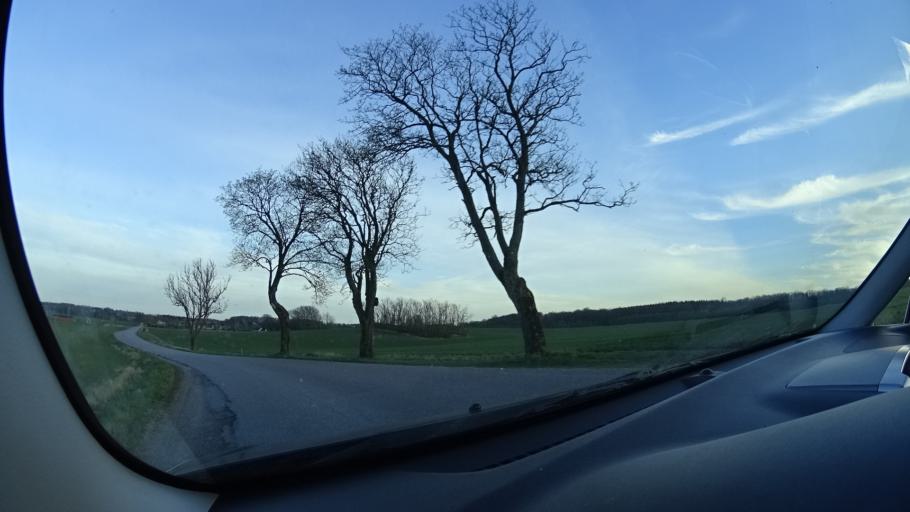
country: SE
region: Skane
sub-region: Eslovs Kommun
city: Stehag
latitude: 55.9111
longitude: 13.3899
